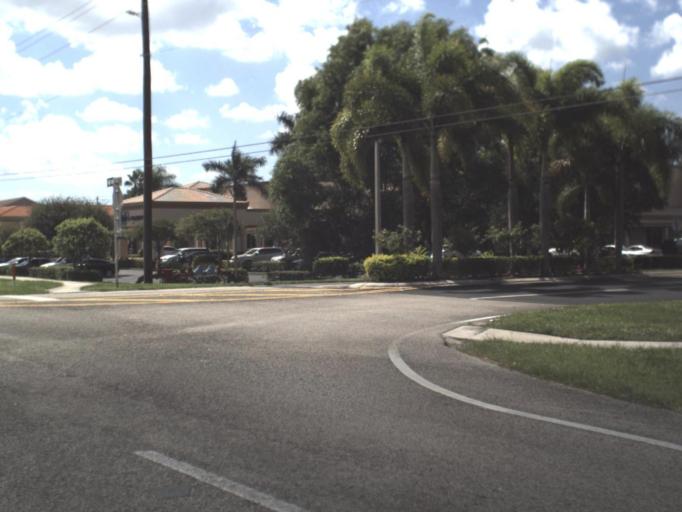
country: US
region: Florida
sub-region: Lee County
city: Bonita Springs
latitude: 26.3110
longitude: -81.8049
